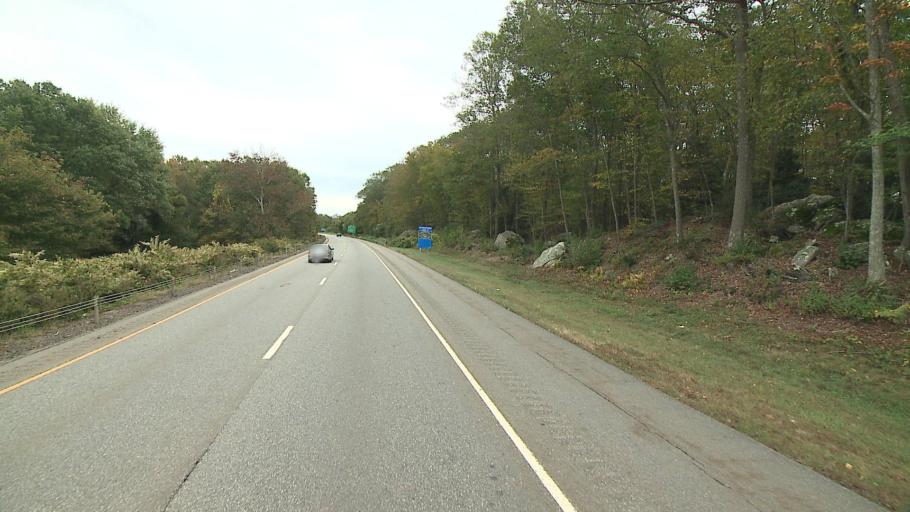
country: US
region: Connecticut
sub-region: Middlesex County
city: Essex Village
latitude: 41.3572
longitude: -72.4172
